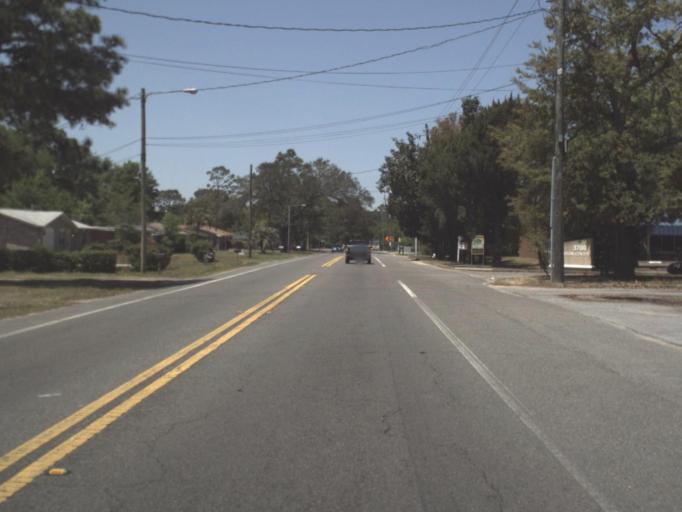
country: US
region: Florida
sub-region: Escambia County
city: Ferry Pass
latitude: 30.4986
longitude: -87.1739
